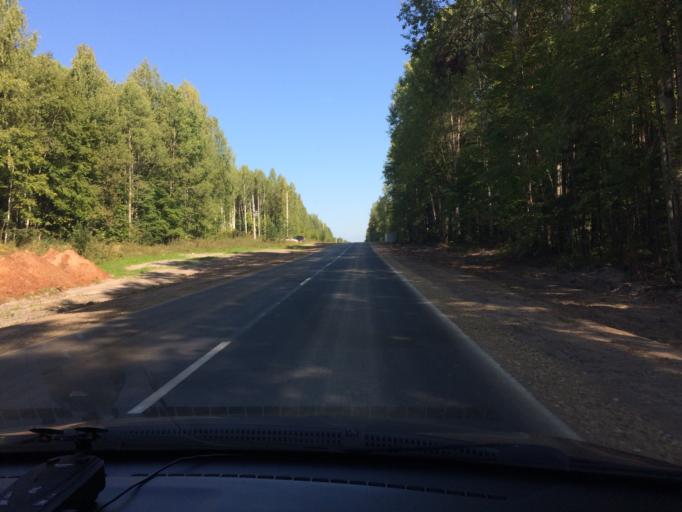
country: RU
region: Mariy-El
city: Sovetskiy
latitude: 56.5551
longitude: 48.4315
